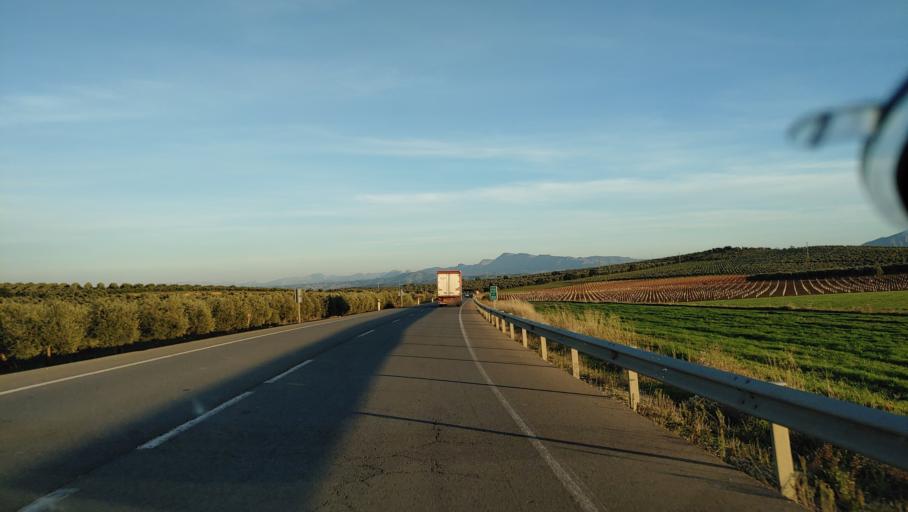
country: ES
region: Andalusia
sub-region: Provincia de Malaga
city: Campillos
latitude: 37.0518
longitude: -4.8063
